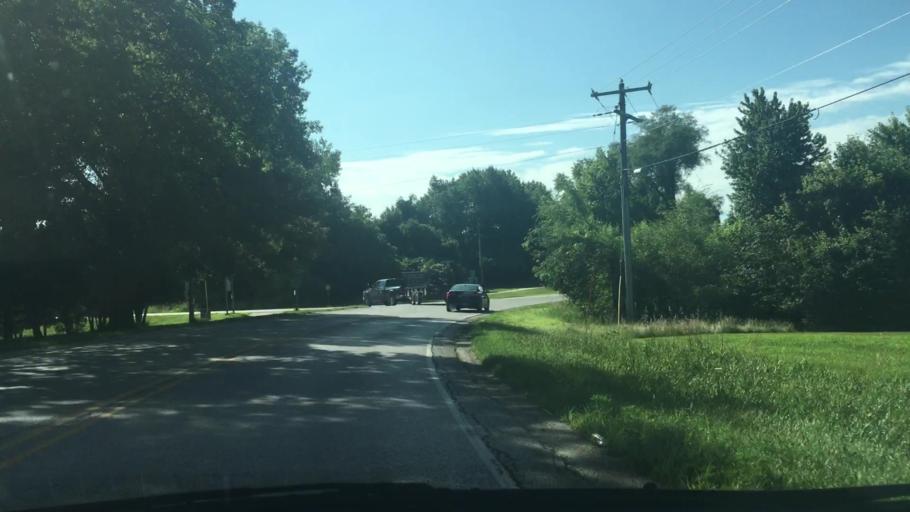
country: US
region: Iowa
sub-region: Johnson County
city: Coralville
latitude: 41.7198
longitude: -91.5545
